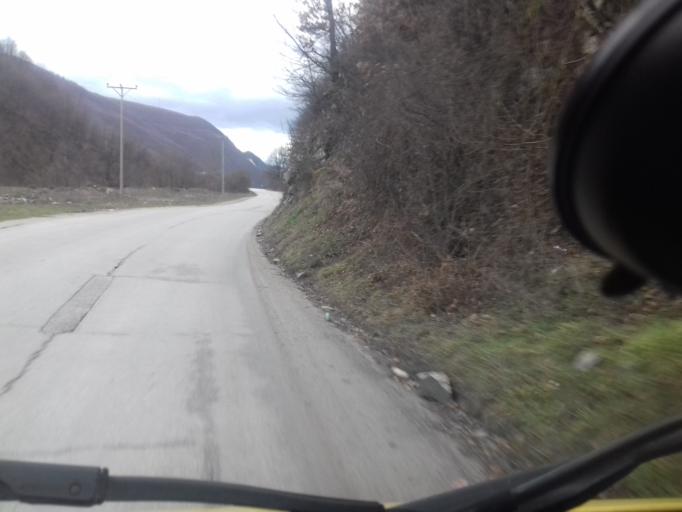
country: BA
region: Federation of Bosnia and Herzegovina
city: Zenica
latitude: 44.2288
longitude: 17.9809
